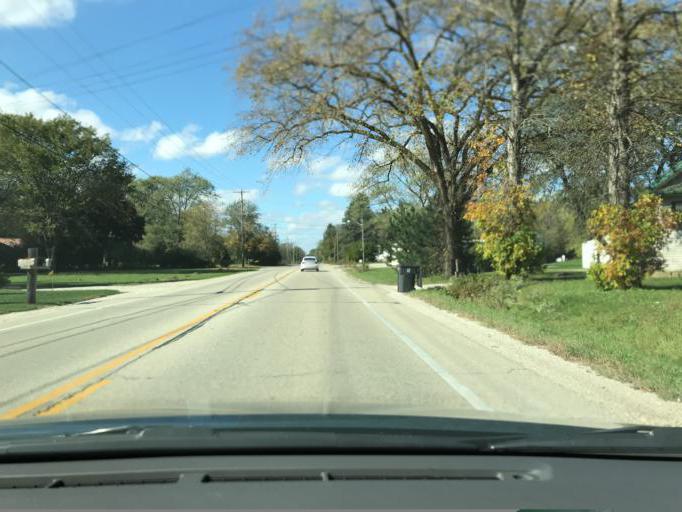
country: US
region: Wisconsin
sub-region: Kenosha County
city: Somers
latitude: 42.6055
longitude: -87.9287
